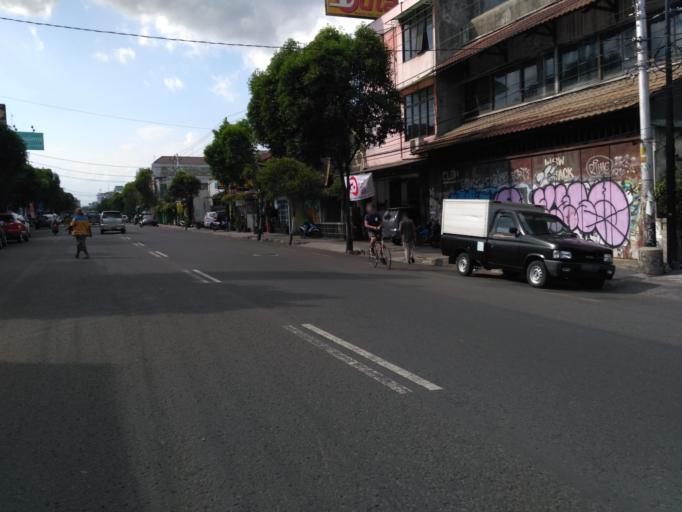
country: ID
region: Daerah Istimewa Yogyakarta
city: Yogyakarta
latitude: -7.8129
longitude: 110.3688
